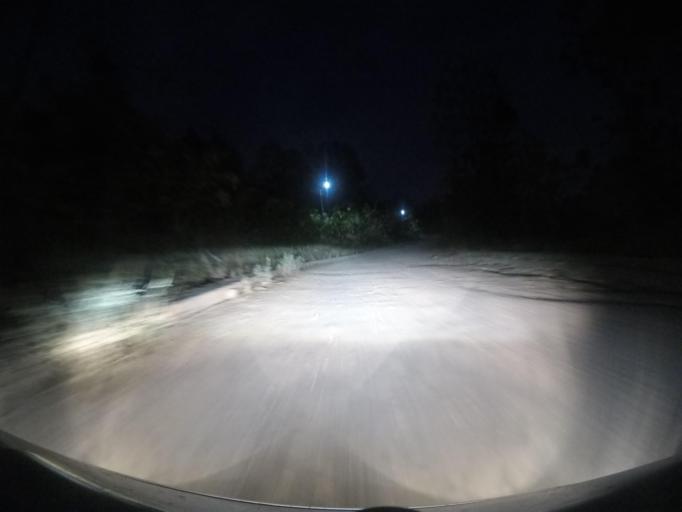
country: TL
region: Viqueque
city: Viqueque
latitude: -8.8466
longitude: 126.3675
